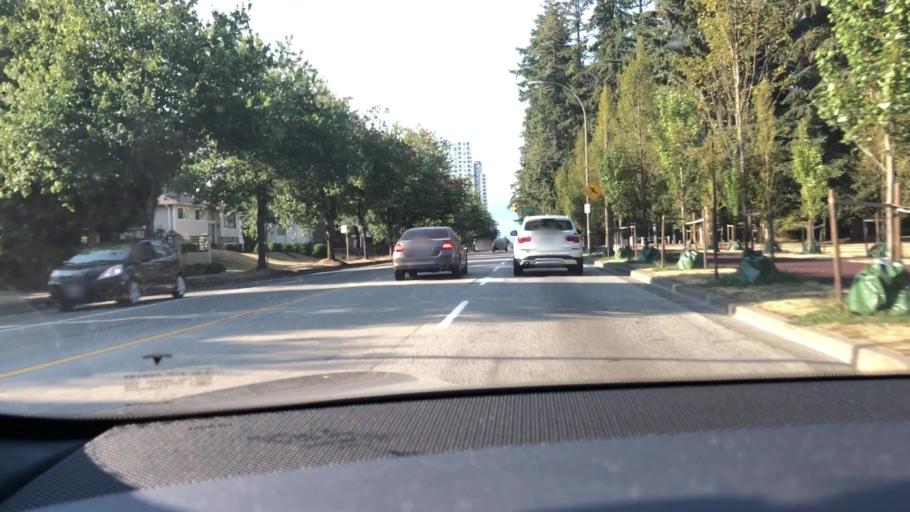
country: CA
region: British Columbia
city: Burnaby
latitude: 49.2282
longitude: -123.0235
